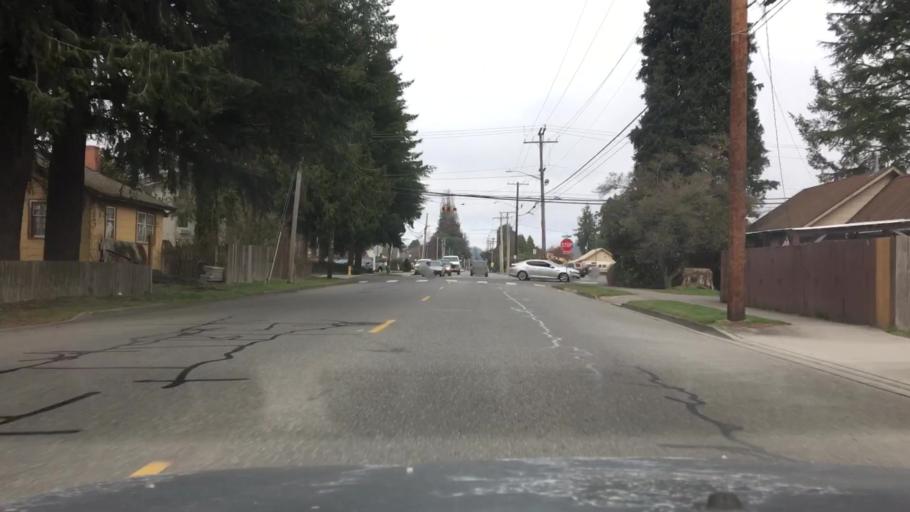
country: US
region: Washington
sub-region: Skagit County
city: Sedro-Woolley
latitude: 48.5028
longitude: -122.2259
